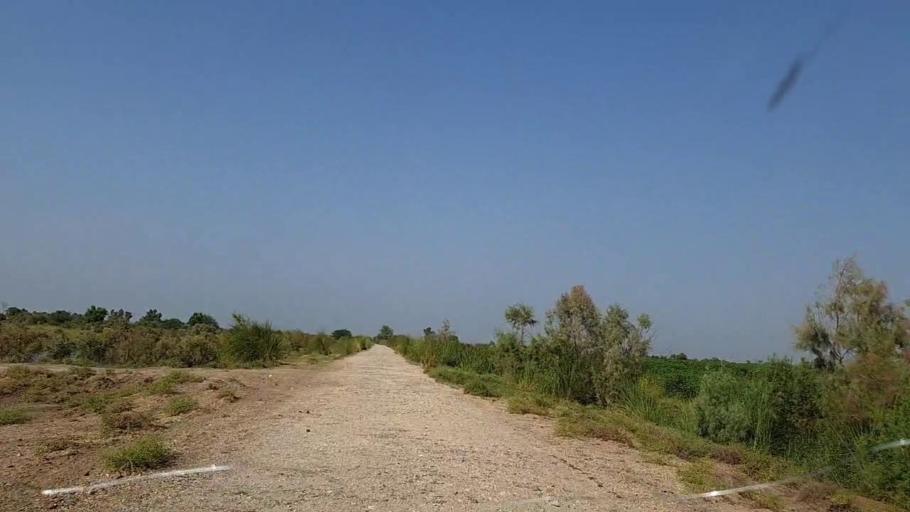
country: PK
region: Sindh
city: Khanpur
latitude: 27.7055
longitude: 69.3871
